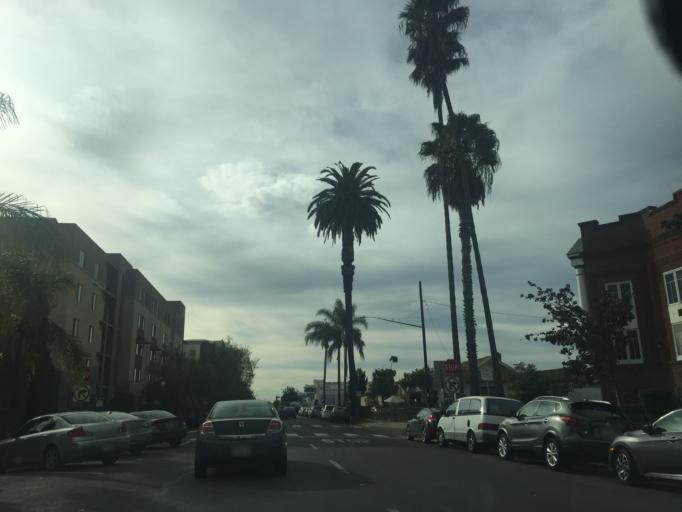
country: US
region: California
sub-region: San Diego County
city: San Diego
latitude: 32.7519
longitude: -117.1020
